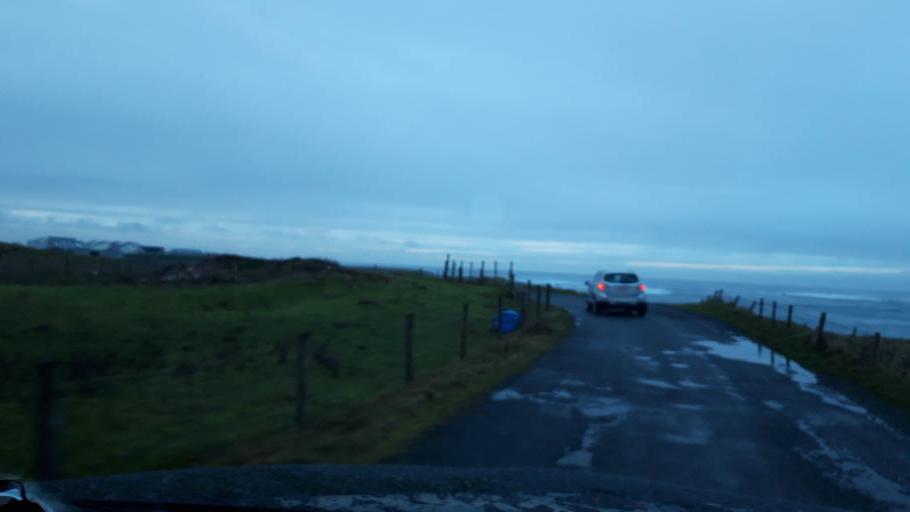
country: IE
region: Ulster
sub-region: County Donegal
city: Ramelton
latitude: 55.2611
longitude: -7.6840
